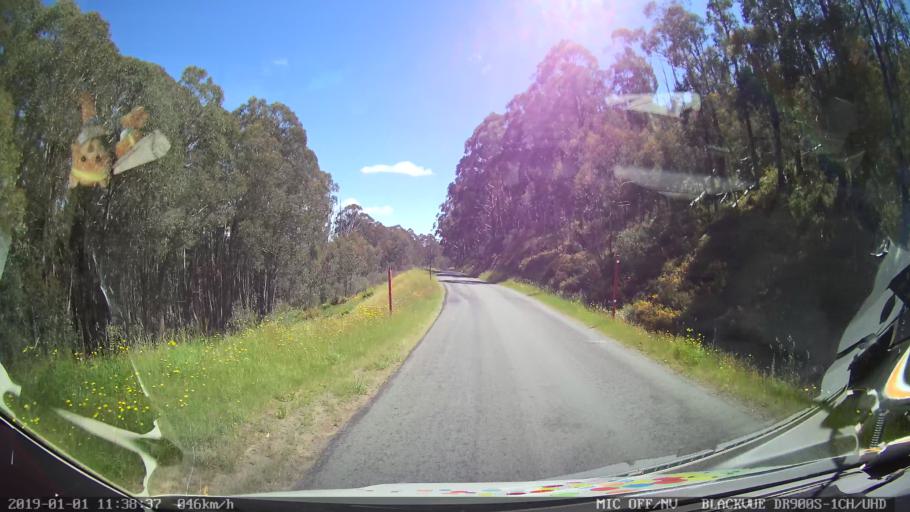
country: AU
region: New South Wales
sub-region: Snowy River
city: Jindabyne
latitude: -35.9331
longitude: 148.3868
